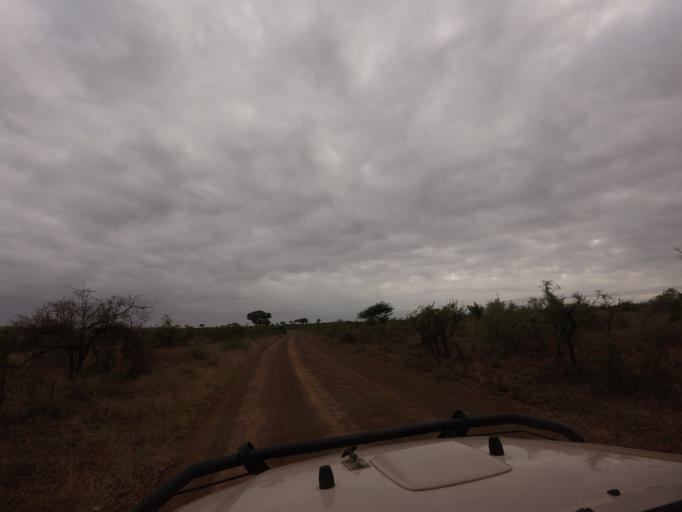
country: ZA
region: Mpumalanga
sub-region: Ehlanzeni District
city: Komatipoort
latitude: -25.3155
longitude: 31.9103
